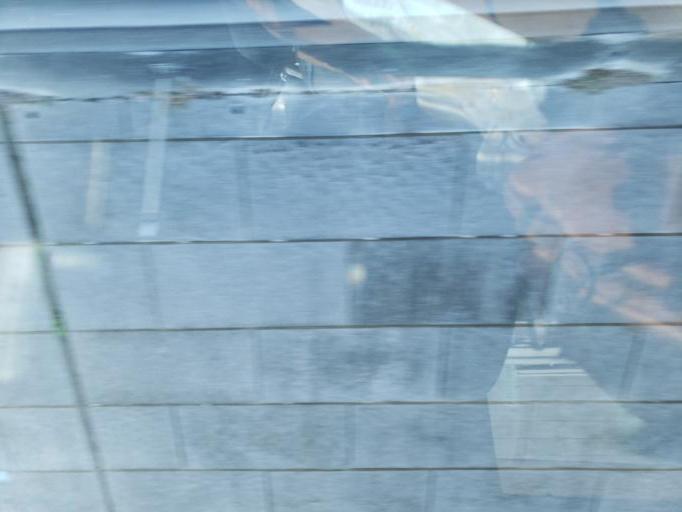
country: JP
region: Hyogo
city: Akashi
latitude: 34.5980
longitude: 135.0069
